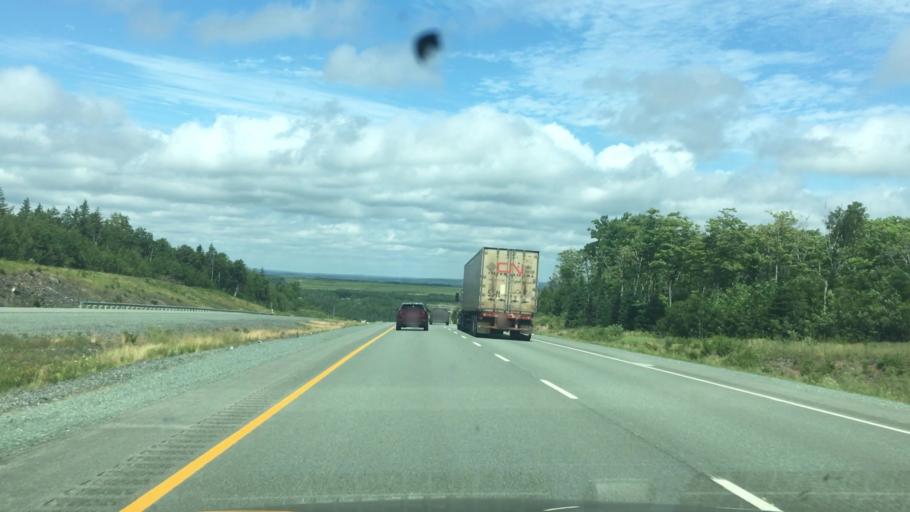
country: CA
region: Nova Scotia
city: Oxford
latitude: 45.5941
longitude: -63.7263
